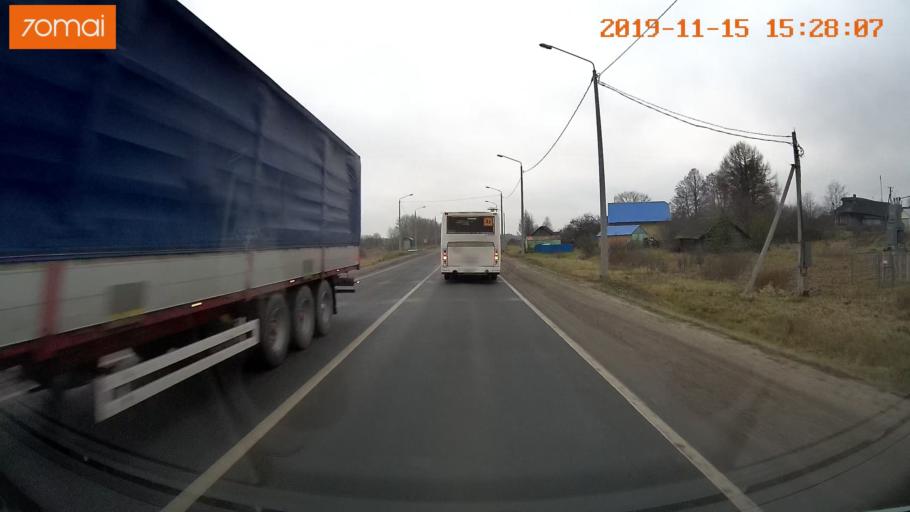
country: RU
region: Jaroslavl
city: Danilov
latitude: 58.1348
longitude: 40.1375
